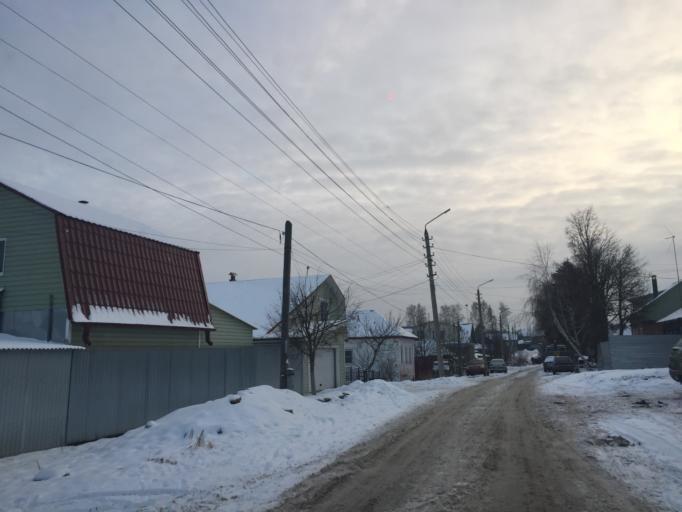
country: RU
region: Tula
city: Gorelki
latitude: 54.2331
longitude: 37.6384
